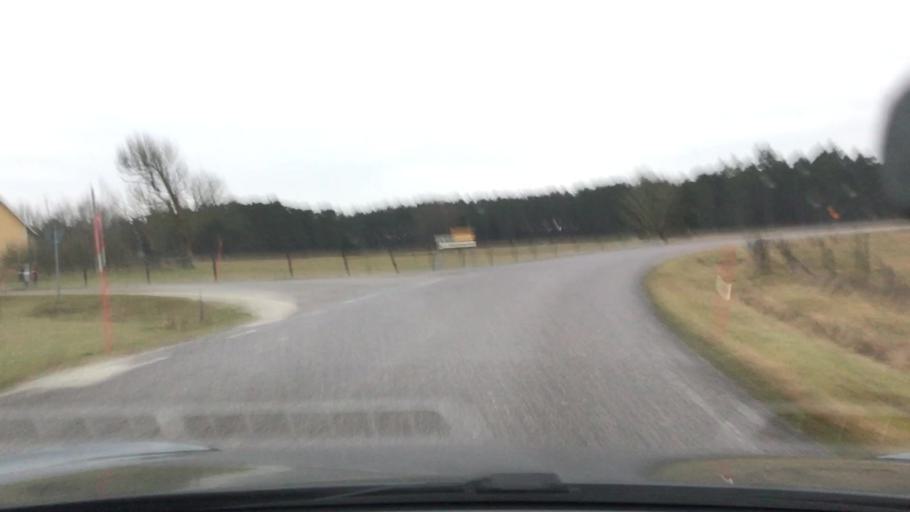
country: SE
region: Gotland
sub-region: Gotland
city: Slite
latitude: 57.3954
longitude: 18.8066
